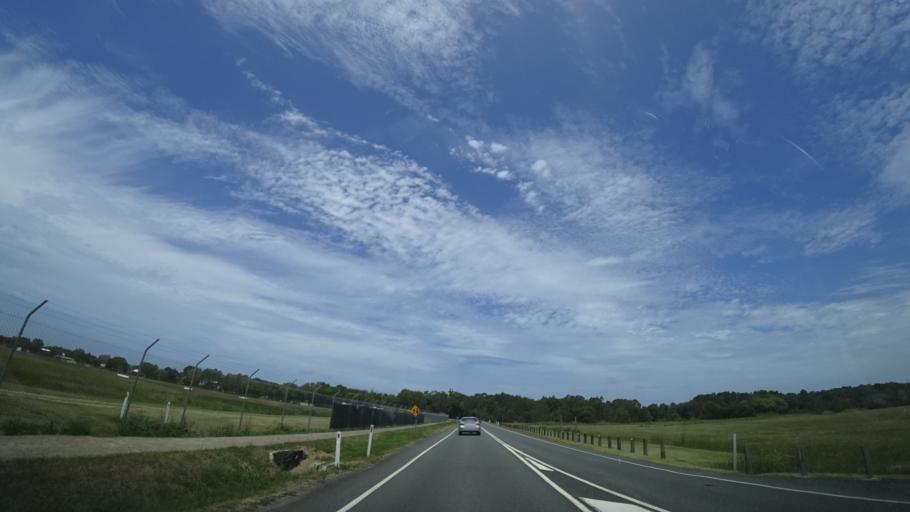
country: AU
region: Queensland
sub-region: Sunshine Coast
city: Mooloolaba
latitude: -26.6112
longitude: 153.0891
